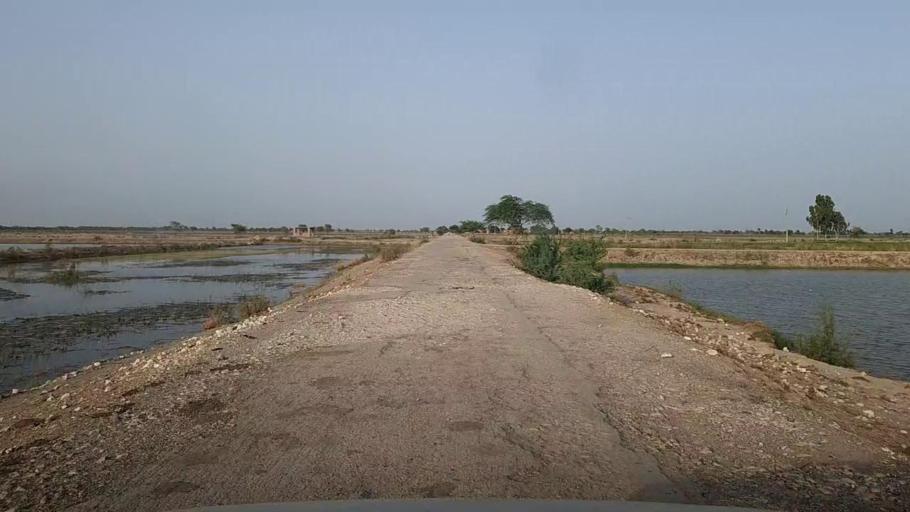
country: PK
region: Sindh
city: Mehar
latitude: 27.1629
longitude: 67.7684
